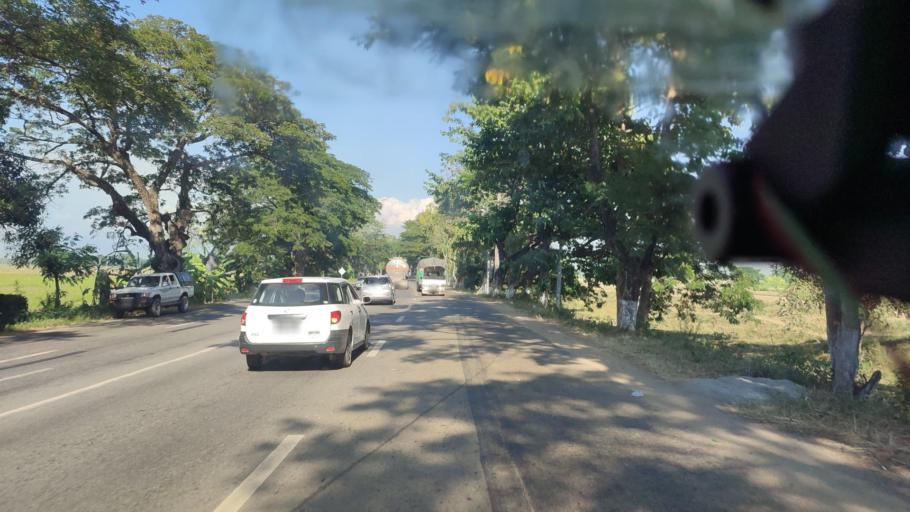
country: MM
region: Mandalay
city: Pyinmana
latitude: 19.7760
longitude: 96.2573
